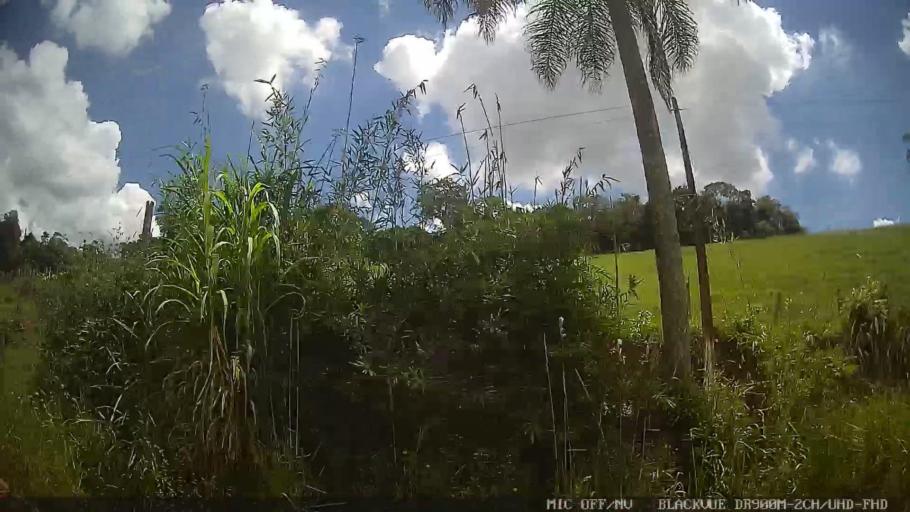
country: BR
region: Sao Paulo
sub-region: Jarinu
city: Jarinu
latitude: -23.1353
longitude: -46.6491
